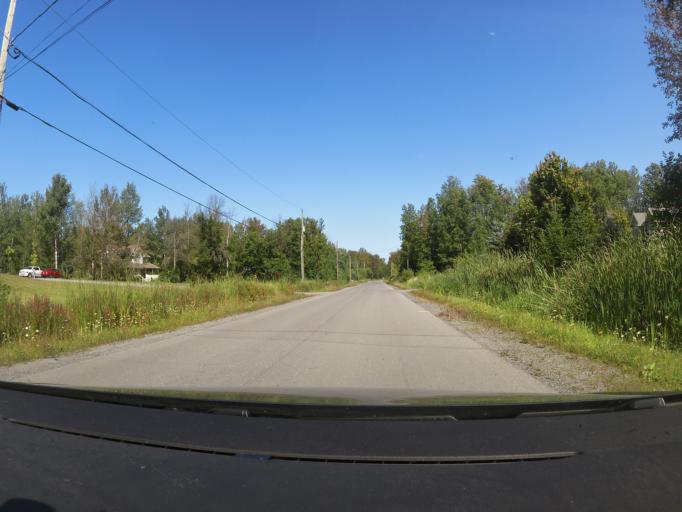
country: CA
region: Ontario
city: Bells Corners
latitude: 45.2834
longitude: -75.9960
